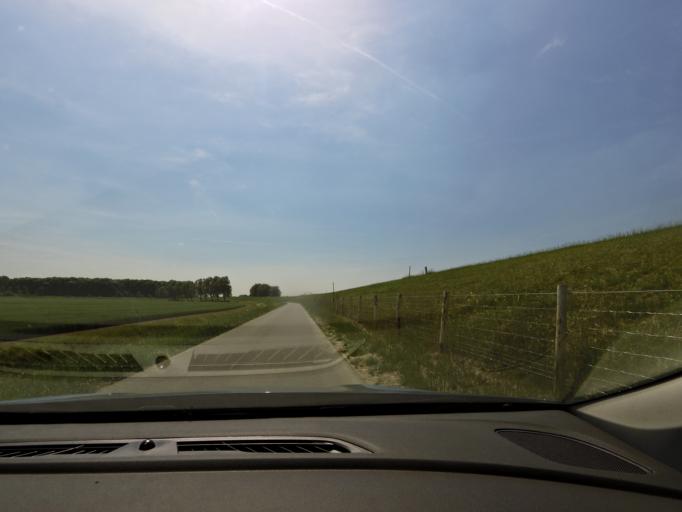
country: NL
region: South Holland
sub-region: Gemeente Spijkenisse
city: Spijkenisse
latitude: 51.8057
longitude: 4.3035
